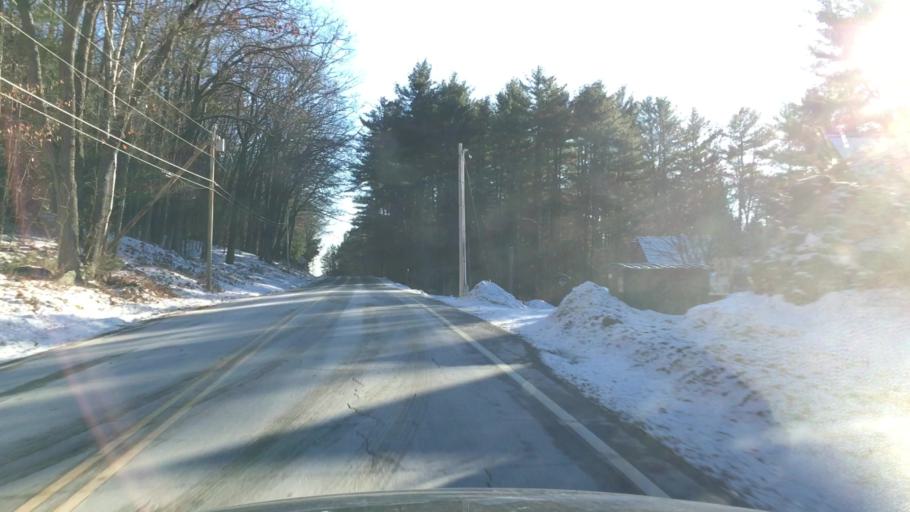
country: US
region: New Hampshire
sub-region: Grafton County
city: Woodsville
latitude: 44.1854
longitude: -72.0512
